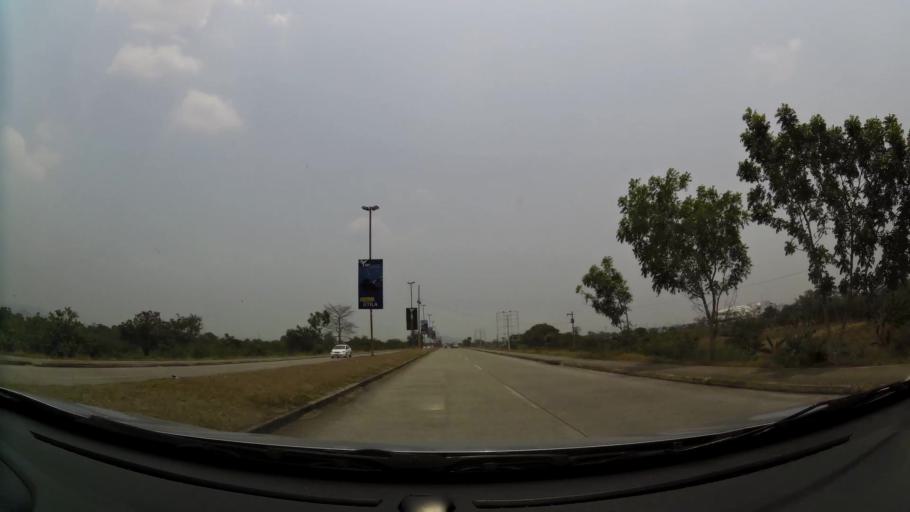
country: HN
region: Cortes
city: La Lima
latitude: 15.4549
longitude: -87.9321
